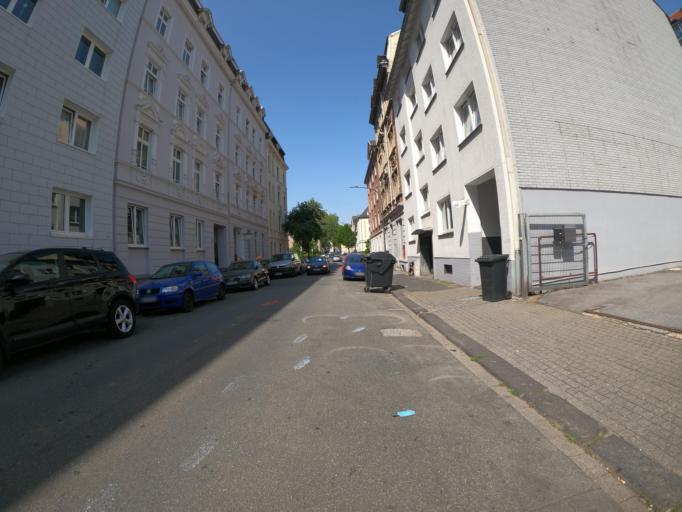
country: DE
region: North Rhine-Westphalia
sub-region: Regierungsbezirk Dusseldorf
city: Wuppertal
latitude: 51.2663
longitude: 7.1525
